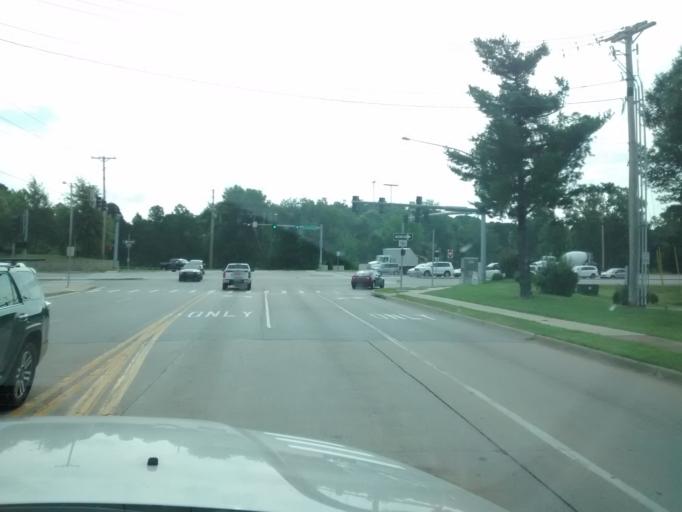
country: US
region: Arkansas
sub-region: Washington County
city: Johnson
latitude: 36.1198
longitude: -94.1193
